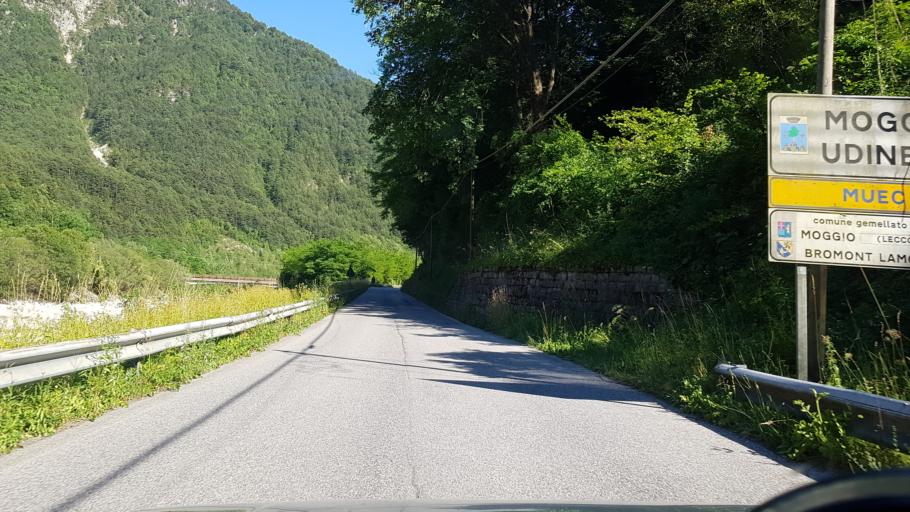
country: IT
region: Friuli Venezia Giulia
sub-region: Provincia di Udine
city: Moggio Udinese
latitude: 46.4165
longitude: 13.1985
